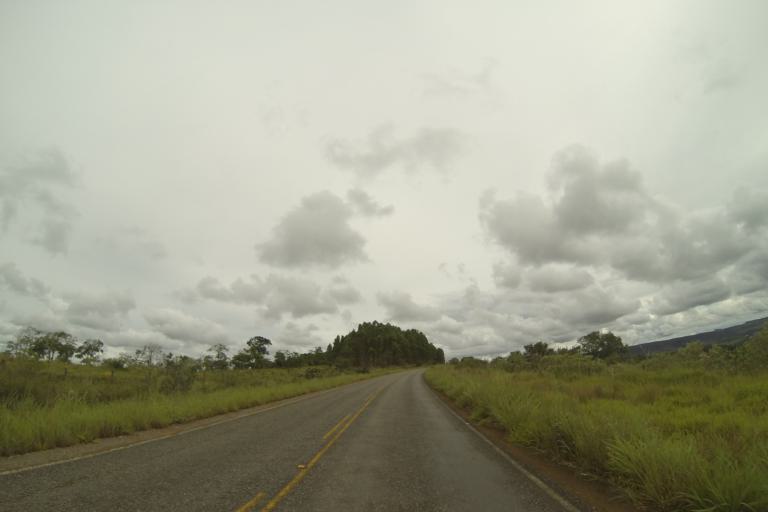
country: BR
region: Minas Gerais
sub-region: Ibia
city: Ibia
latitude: -19.6894
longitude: -46.4434
